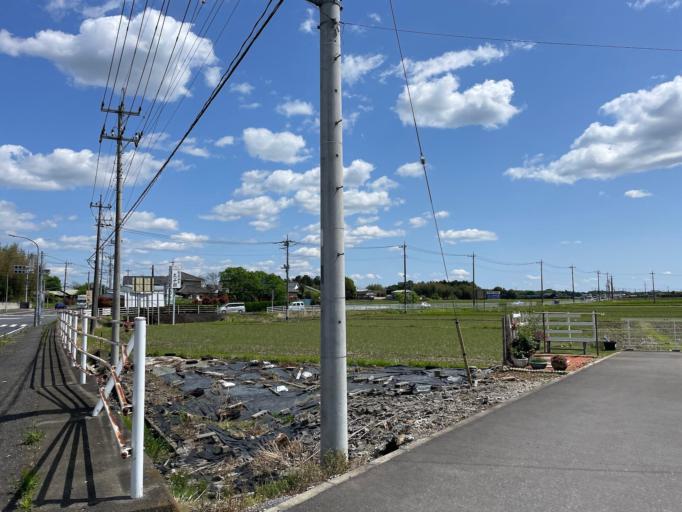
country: JP
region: Tochigi
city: Sano
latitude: 36.3243
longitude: 139.6377
